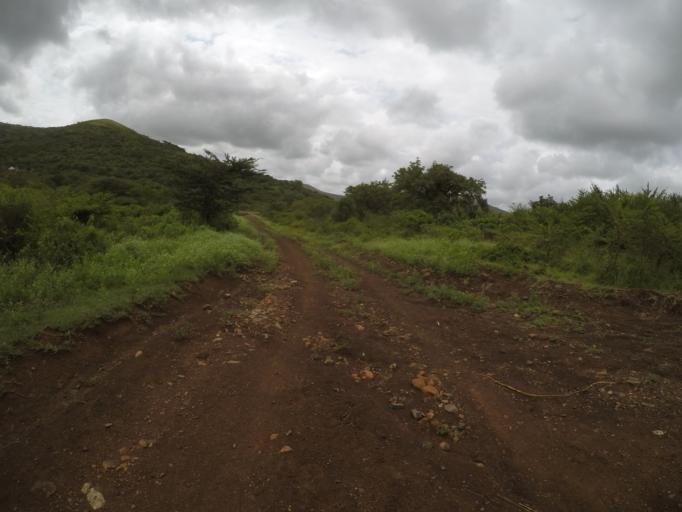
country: ZA
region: KwaZulu-Natal
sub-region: uThungulu District Municipality
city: Empangeni
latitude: -28.5833
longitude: 31.8876
